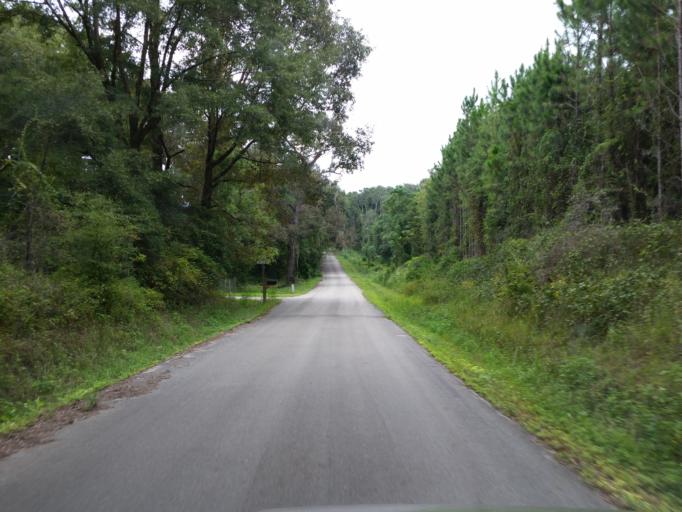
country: US
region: Florida
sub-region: Alachua County
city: High Springs
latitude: 29.9817
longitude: -82.5636
